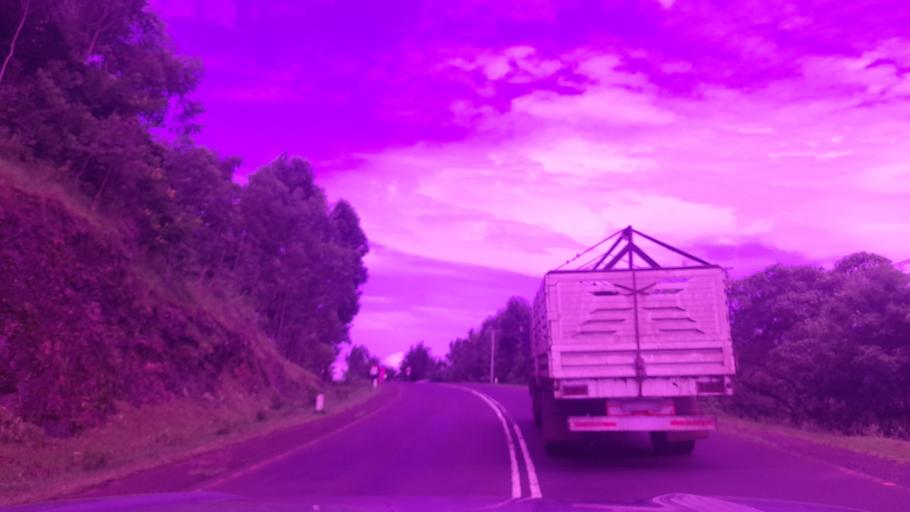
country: ET
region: Oromiya
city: Jima
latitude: 7.5220
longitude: 36.5379
